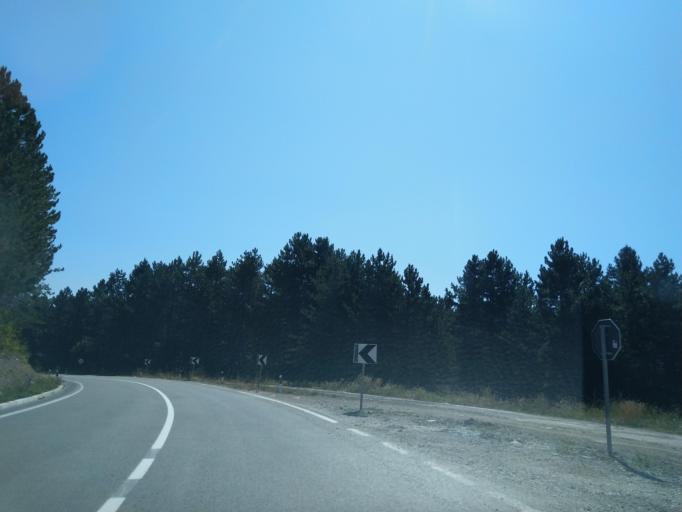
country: RS
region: Central Serbia
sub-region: Zlatiborski Okrug
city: Sjenica
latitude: 43.3060
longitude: 19.9013
